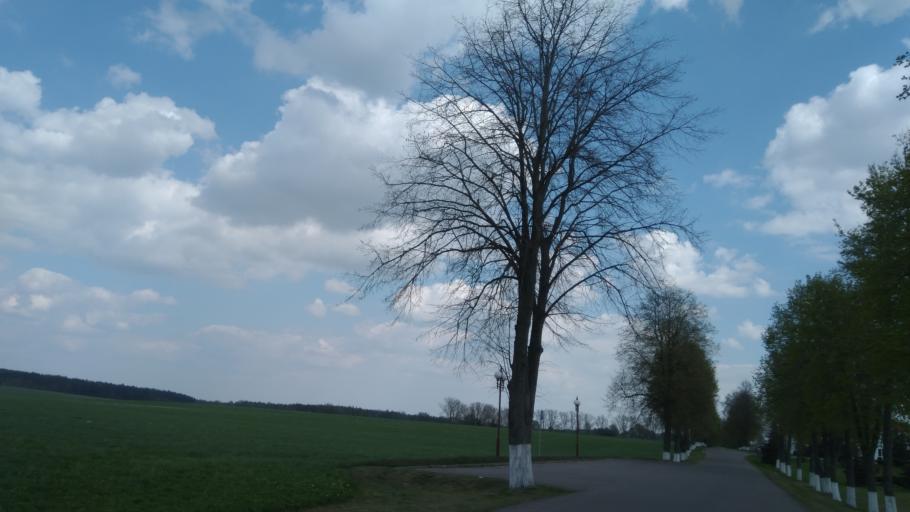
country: BY
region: Minsk
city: Nyasvizh
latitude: 53.2474
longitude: 26.6843
